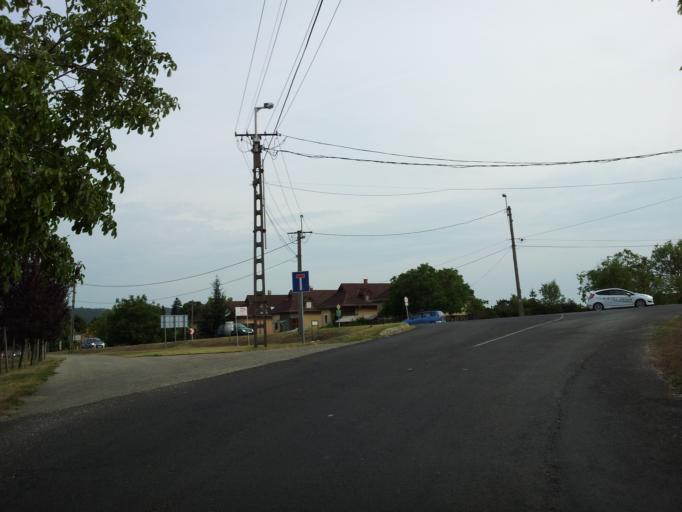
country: HU
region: Veszprem
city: Balatonfured
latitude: 46.9282
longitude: 17.8348
